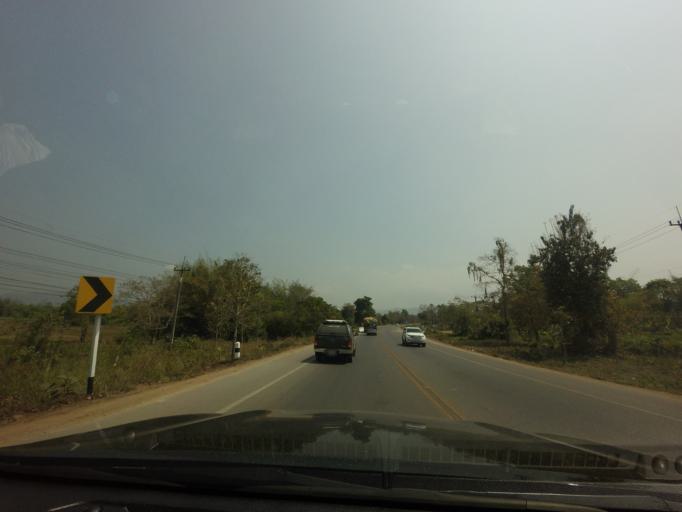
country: TH
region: Kanchanaburi
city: Thong Pha Phum
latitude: 14.6451
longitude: 98.6965
